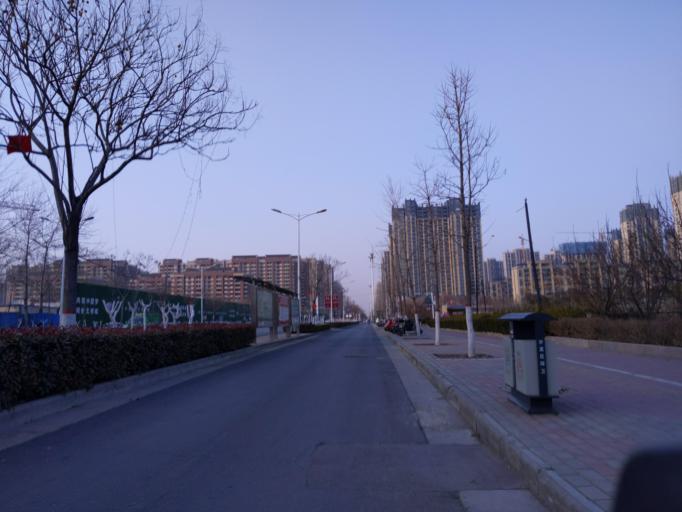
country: CN
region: Henan Sheng
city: Puyang
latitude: 35.7845
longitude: 115.0150
